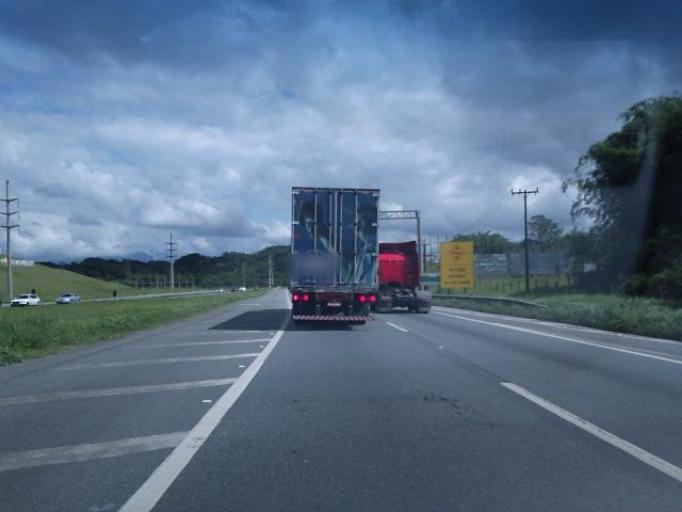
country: BR
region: Santa Catarina
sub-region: Joinville
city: Joinville
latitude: -26.3675
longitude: -48.8577
